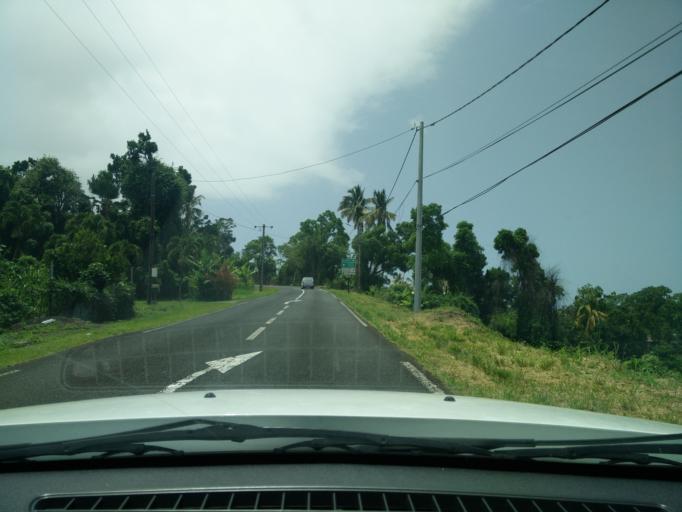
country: GP
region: Guadeloupe
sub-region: Guadeloupe
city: Trois-Rivieres
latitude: 15.9803
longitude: -61.6275
